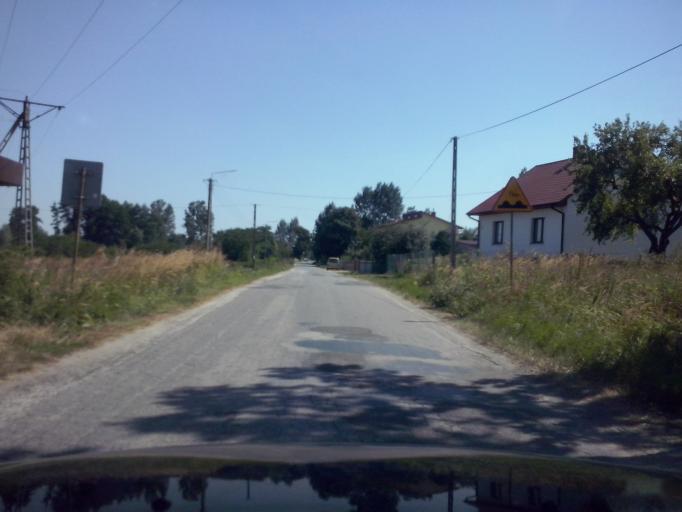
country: PL
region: Swietokrzyskie
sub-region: Powiat kielecki
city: Chmielnik
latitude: 50.6023
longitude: 20.7980
